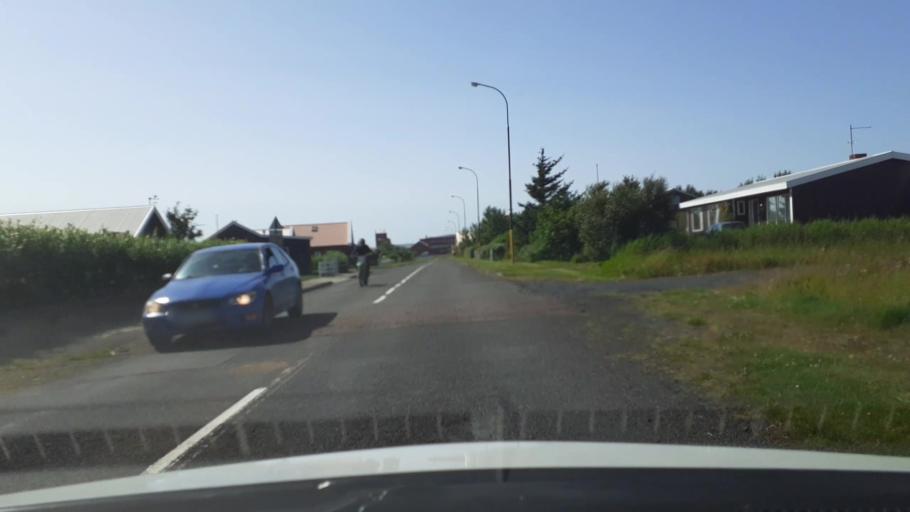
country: IS
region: South
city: Selfoss
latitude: 63.8388
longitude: -21.0573
